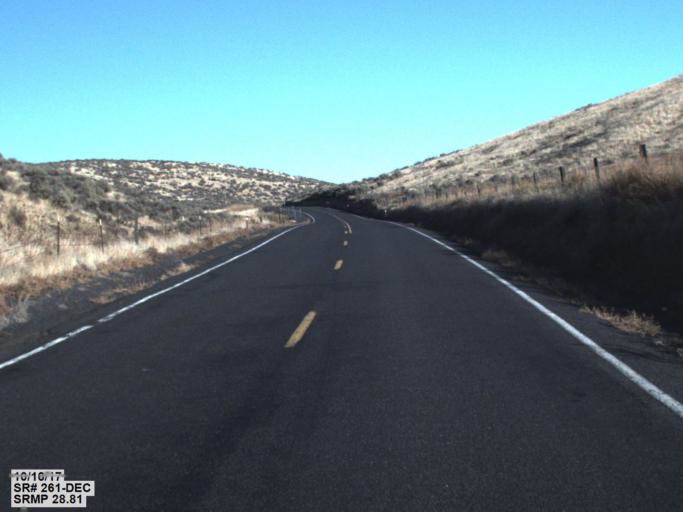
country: US
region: Washington
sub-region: Adams County
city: Ritzville
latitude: 46.6986
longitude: -118.4015
